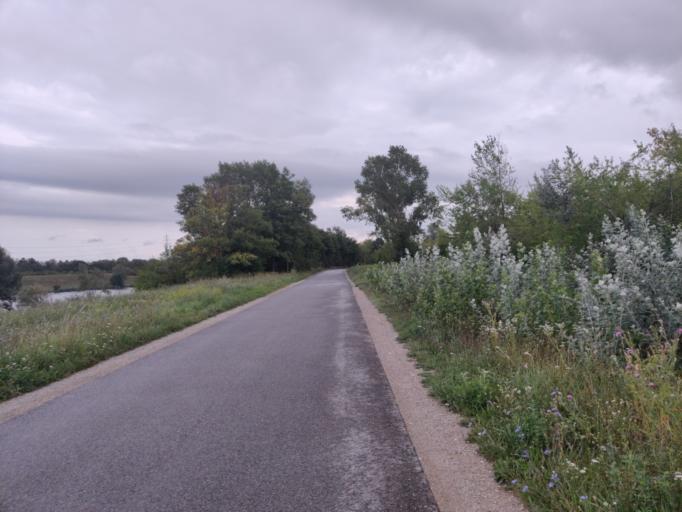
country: AT
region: Lower Austria
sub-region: Politischer Bezirk Korneuburg
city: Langenzersdorf
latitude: 48.2740
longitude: 16.3652
